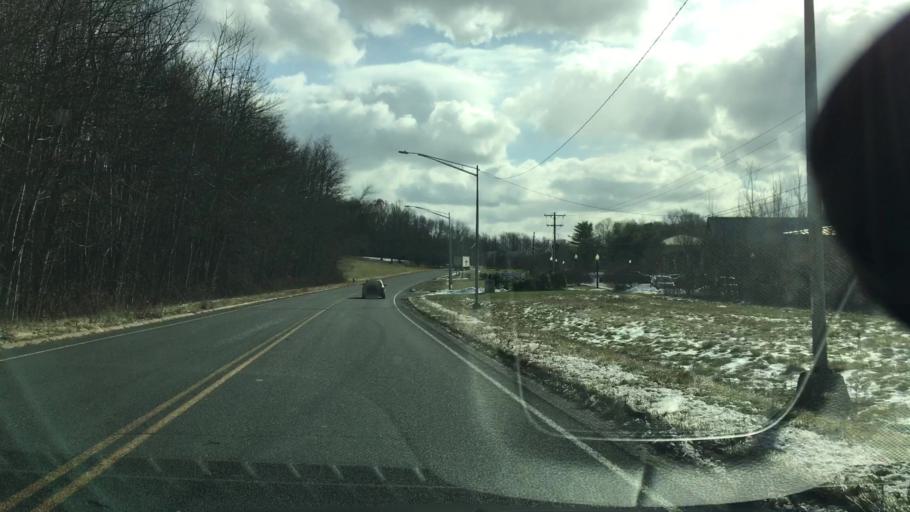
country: US
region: Connecticut
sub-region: New Haven County
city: Meriden
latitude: 41.5043
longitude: -72.7655
